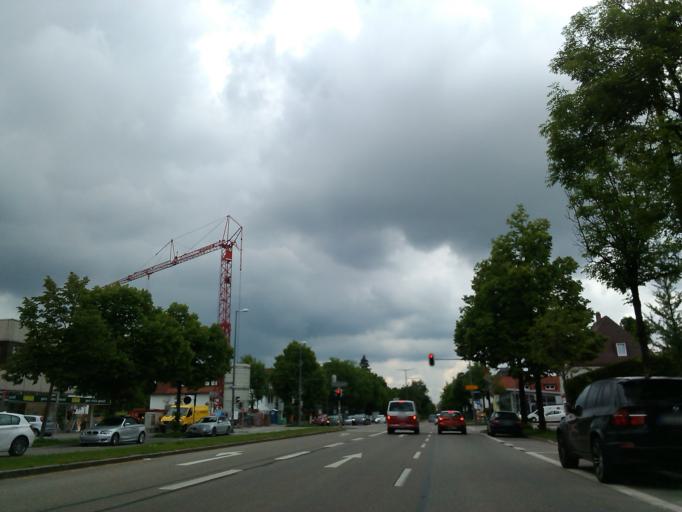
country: DE
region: Bavaria
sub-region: Upper Bavaria
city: Haar
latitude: 48.1152
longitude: 11.6960
